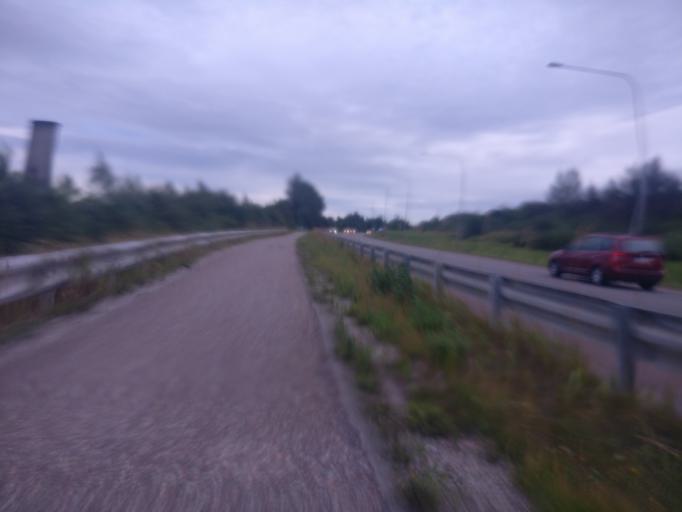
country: SE
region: Vaesternorrland
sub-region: Sundsvalls Kommun
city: Stockvik
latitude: 62.3710
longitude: 17.3679
